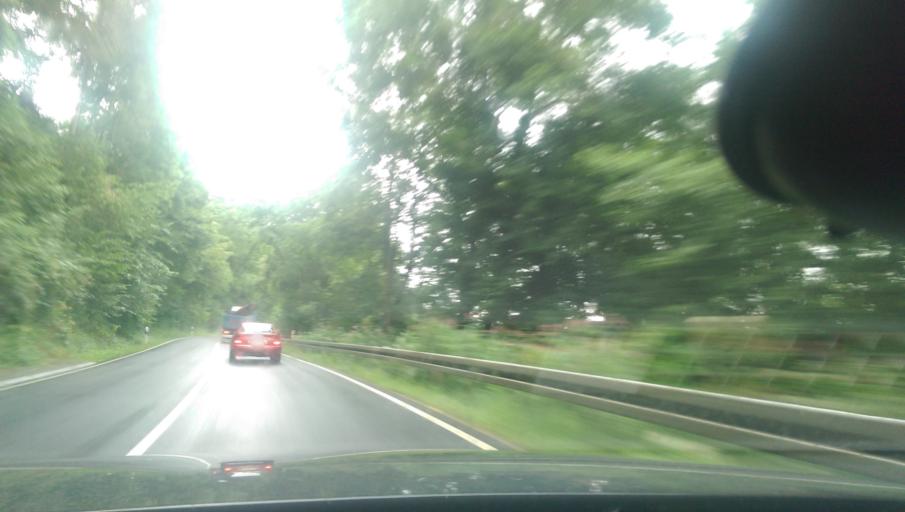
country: DE
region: Hesse
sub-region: Regierungsbezirk Kassel
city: Grossalmerode
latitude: 51.2770
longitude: 9.8430
